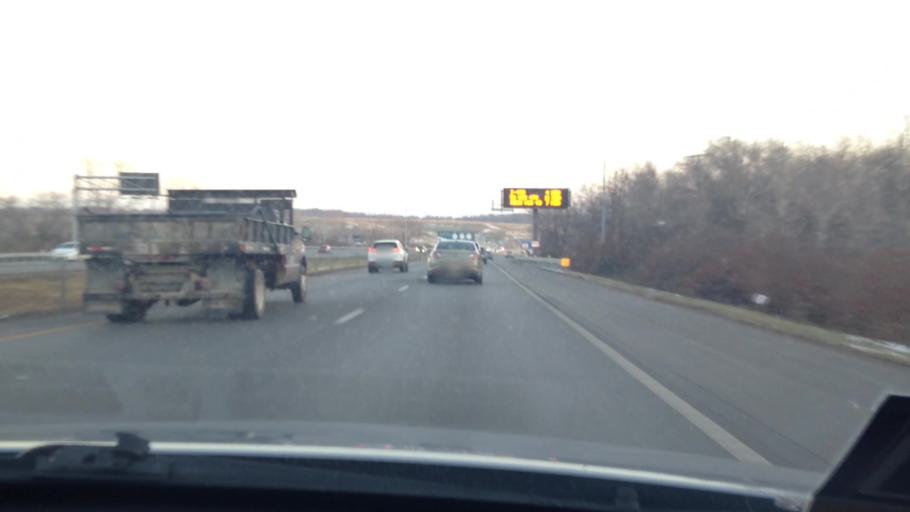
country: US
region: Kansas
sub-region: Johnson County
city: Leawood
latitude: 38.9826
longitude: -94.5492
